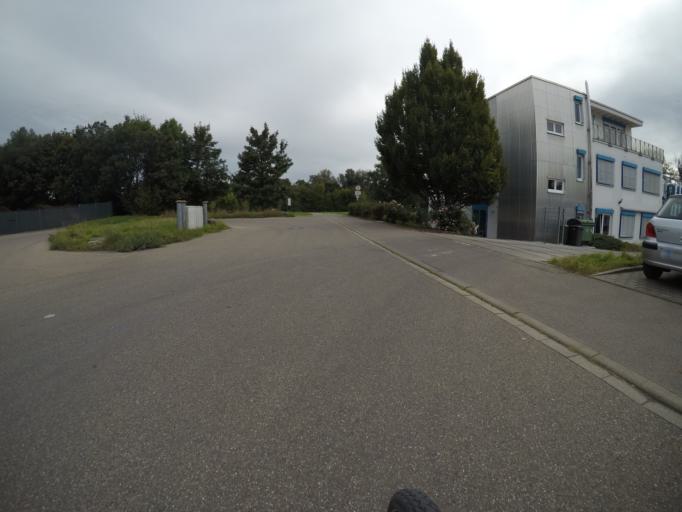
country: DE
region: Baden-Wuerttemberg
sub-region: Regierungsbezirk Stuttgart
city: Marbach am Neckar
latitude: 48.8941
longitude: 9.2606
